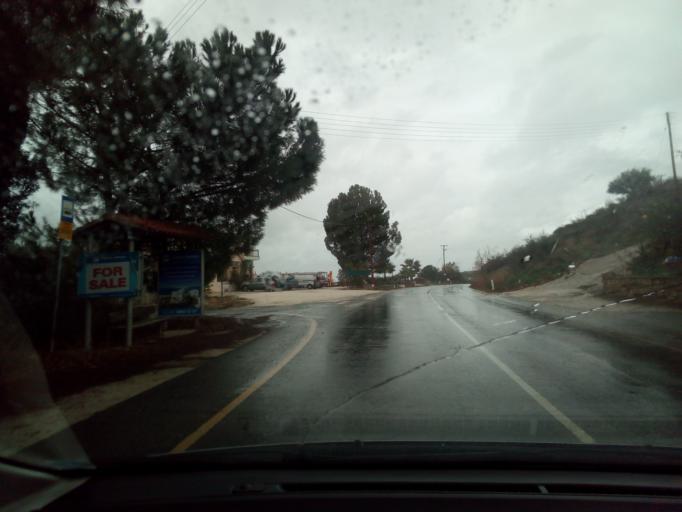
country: CY
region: Pafos
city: Polis
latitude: 34.9875
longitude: 32.4516
